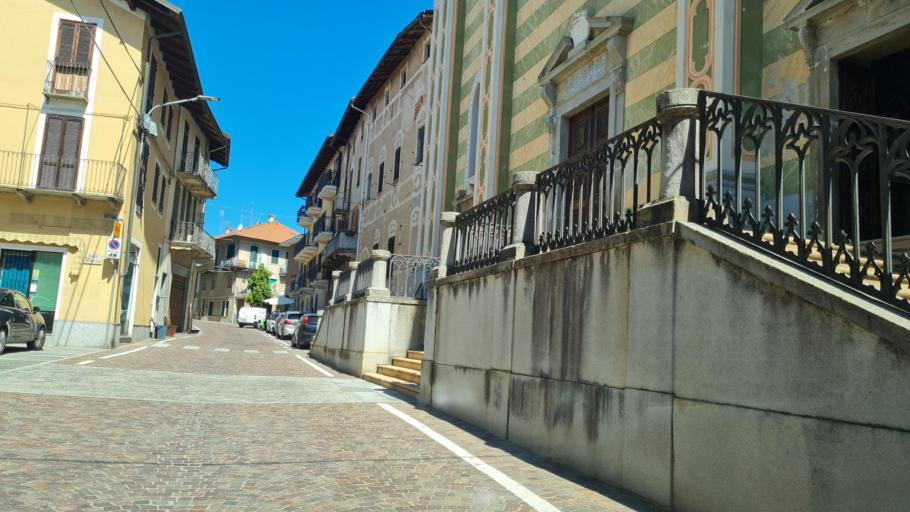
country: IT
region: Piedmont
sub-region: Provincia di Biella
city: Masserano
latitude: 45.5943
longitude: 8.2258
